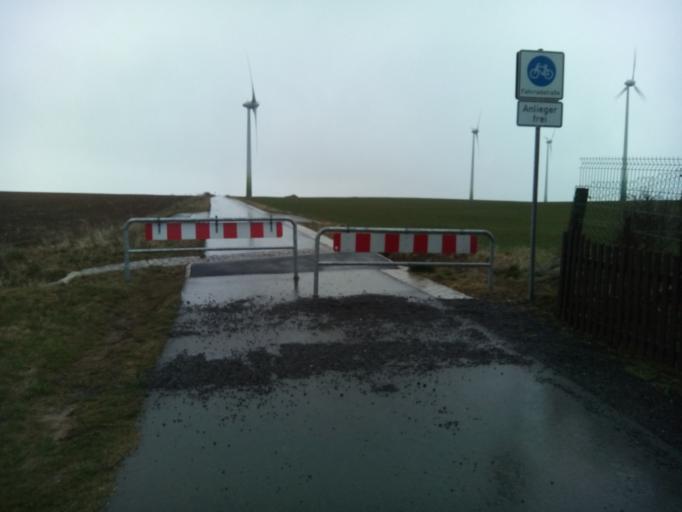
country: DE
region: Saxony
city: Freiberg
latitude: 50.8874
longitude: 13.3595
